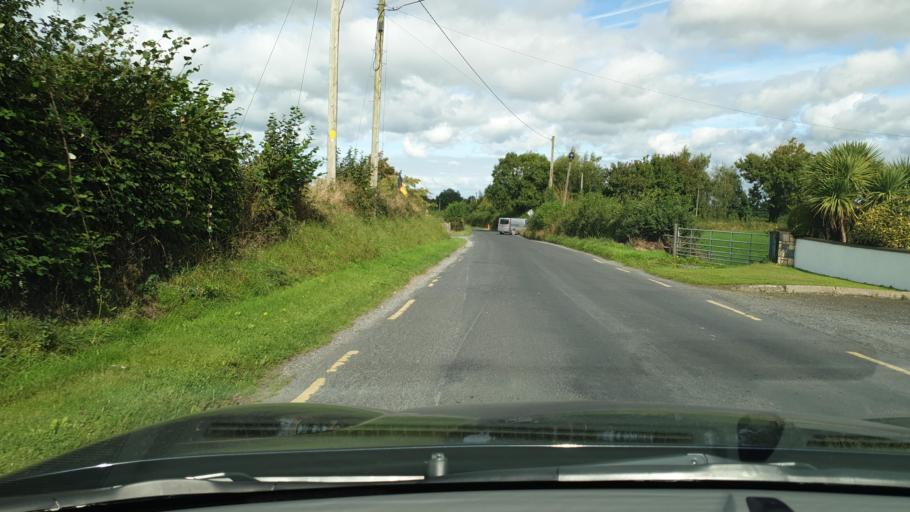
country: IE
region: Leinster
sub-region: Laois
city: Portlaoise
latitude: 53.0598
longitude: -7.2601
